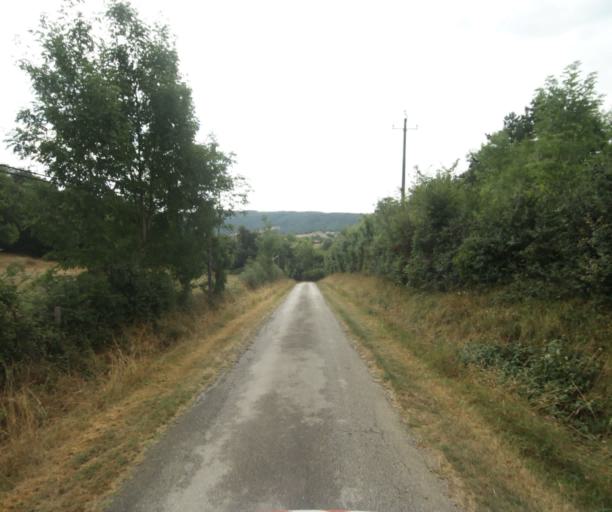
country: FR
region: Midi-Pyrenees
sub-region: Departement de la Haute-Garonne
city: Revel
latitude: 43.4292
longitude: 1.9791
